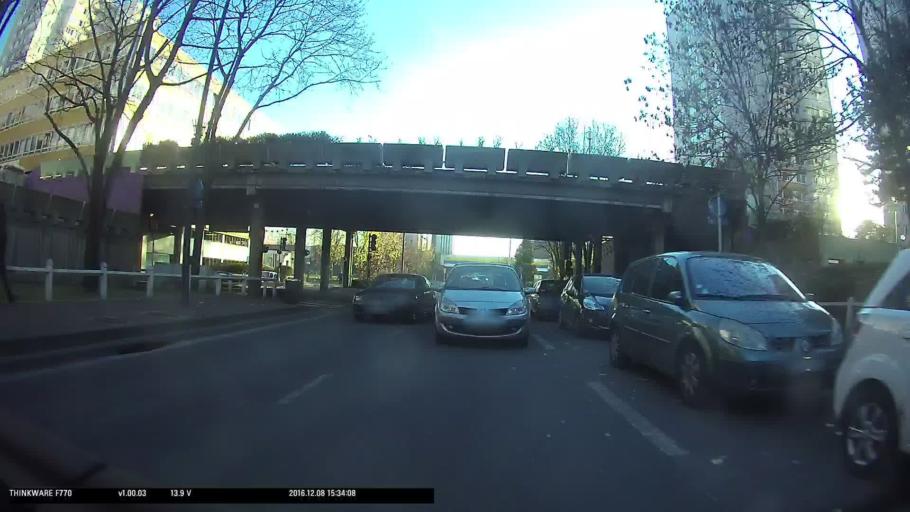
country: FR
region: Ile-de-France
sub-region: Departement de Seine-Saint-Denis
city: Bobigny
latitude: 48.9049
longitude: 2.4457
